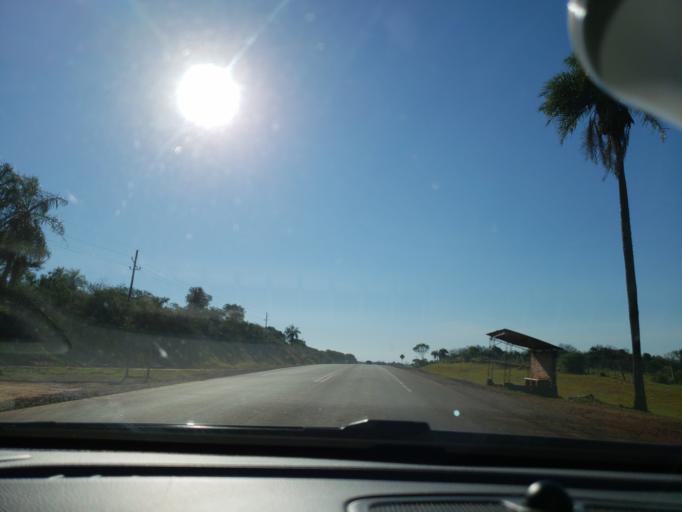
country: AR
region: Misiones
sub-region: Departamento de Apostoles
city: San Jose
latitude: -27.7995
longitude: -55.7697
